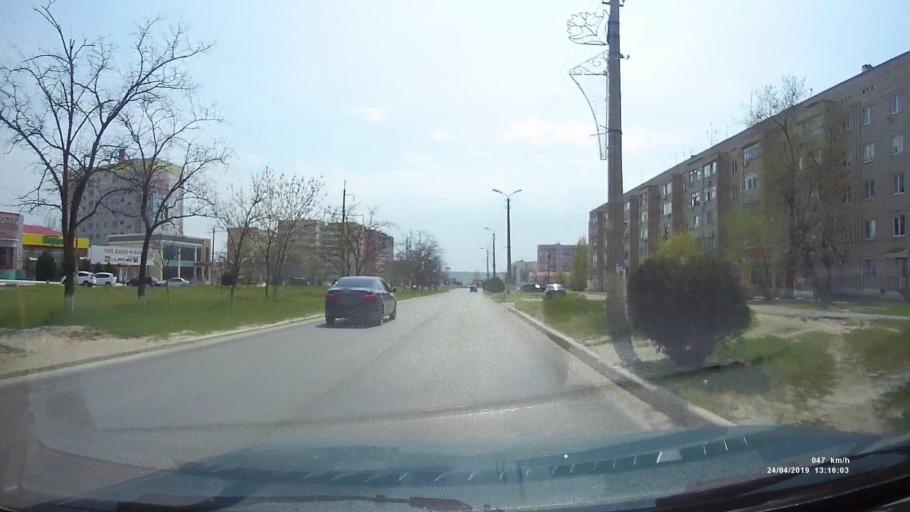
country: RU
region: Kalmykiya
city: Elista
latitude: 46.3059
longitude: 44.3046
